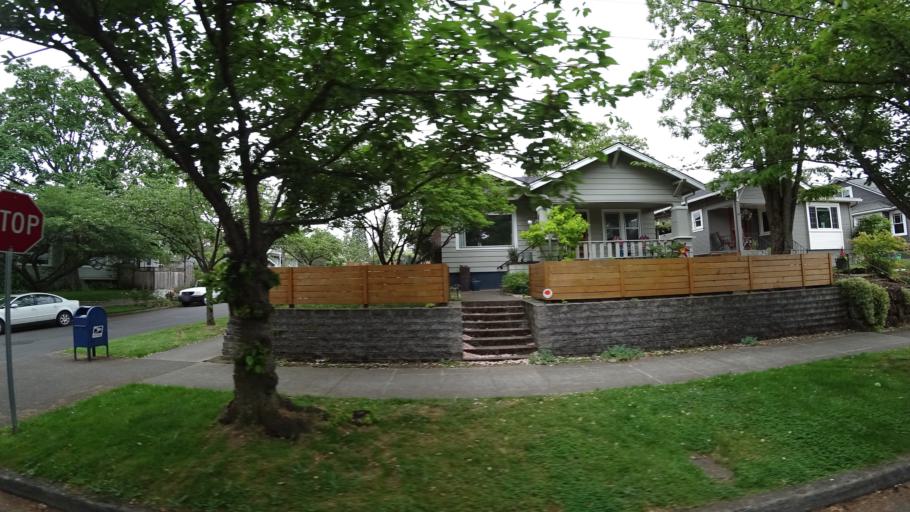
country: US
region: Oregon
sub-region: Multnomah County
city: Portland
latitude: 45.5436
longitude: -122.6158
